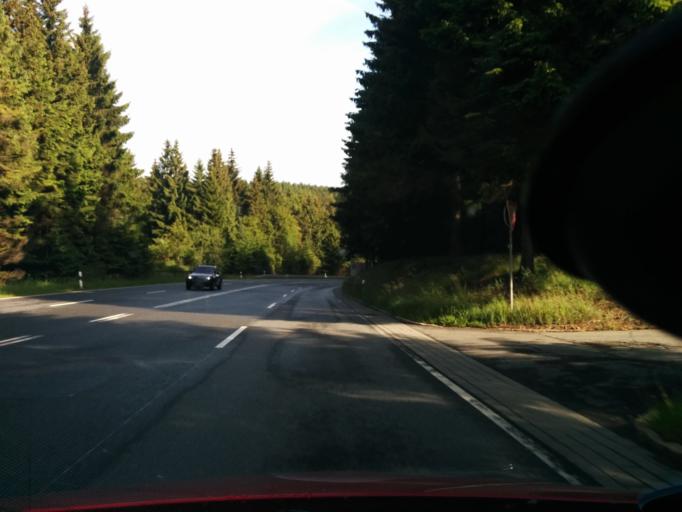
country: DE
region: Lower Saxony
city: Bad Harzburg
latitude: 51.8386
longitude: 10.5287
